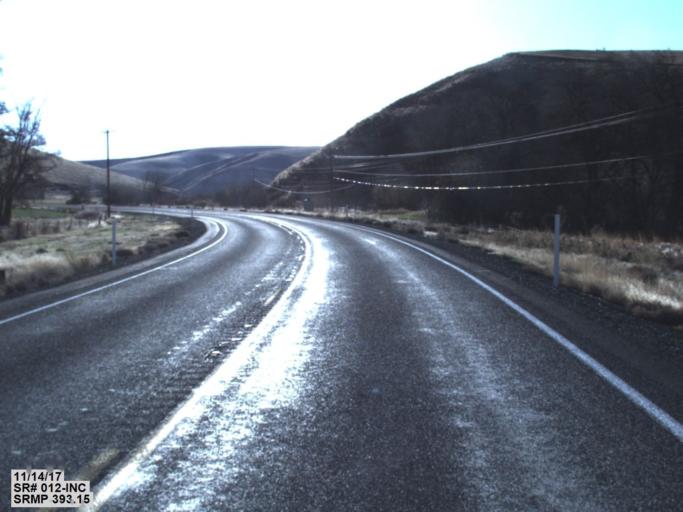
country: US
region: Washington
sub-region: Garfield County
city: Pomeroy
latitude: 46.5075
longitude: -117.7842
